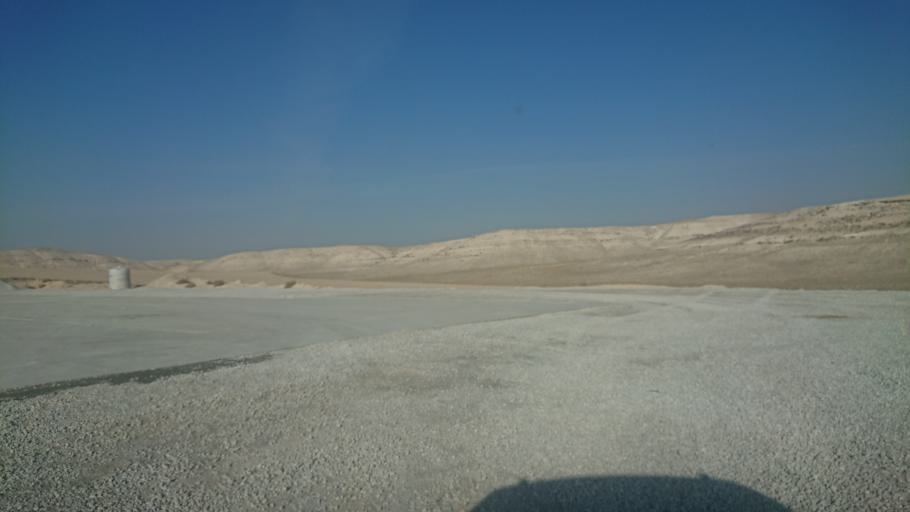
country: TR
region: Aksaray
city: Sultanhani
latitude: 38.0856
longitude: 33.6213
